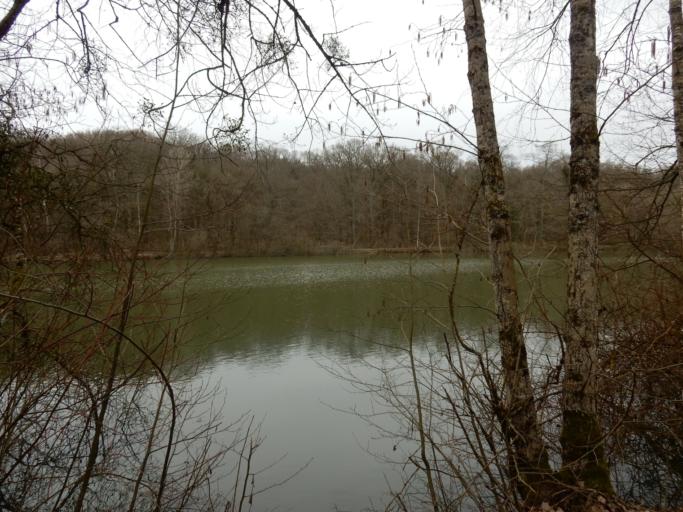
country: LU
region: Luxembourg
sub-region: Canton d'Esch-sur-Alzette
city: Leudelange
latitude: 49.5660
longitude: 6.1047
